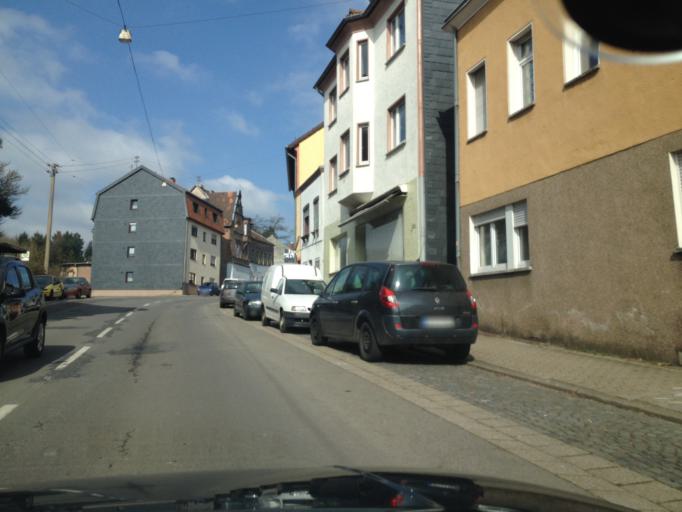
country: DE
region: Saarland
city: Friedrichsthal
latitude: 49.3237
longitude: 7.0982
